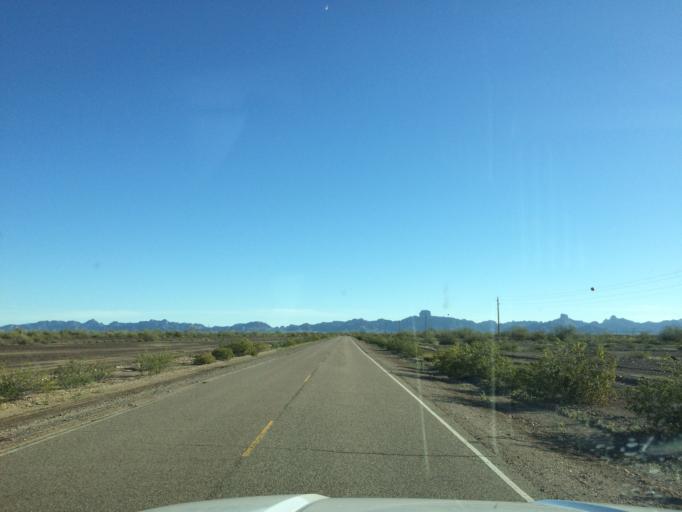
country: US
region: Arizona
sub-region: Yuma County
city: Wellton
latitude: 32.9782
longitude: -114.2754
